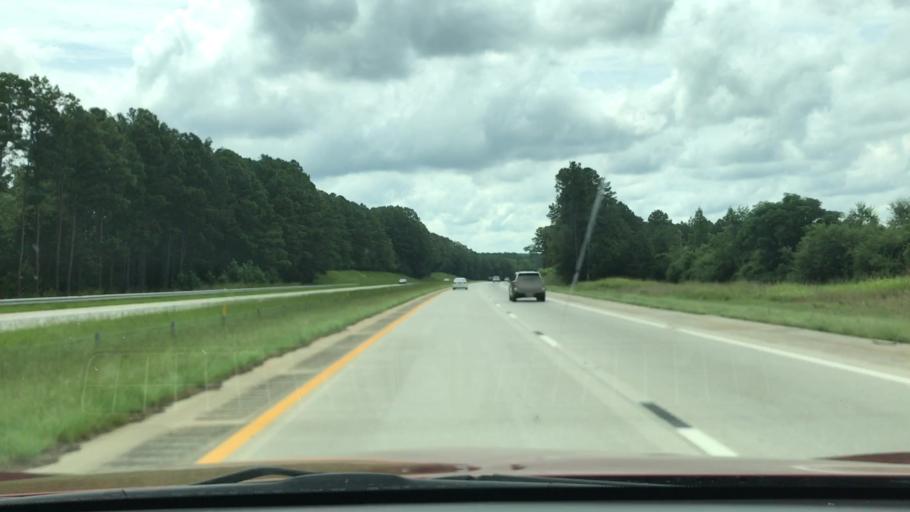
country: US
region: South Carolina
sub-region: Laurens County
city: Laurens
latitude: 34.6051
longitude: -82.0655
